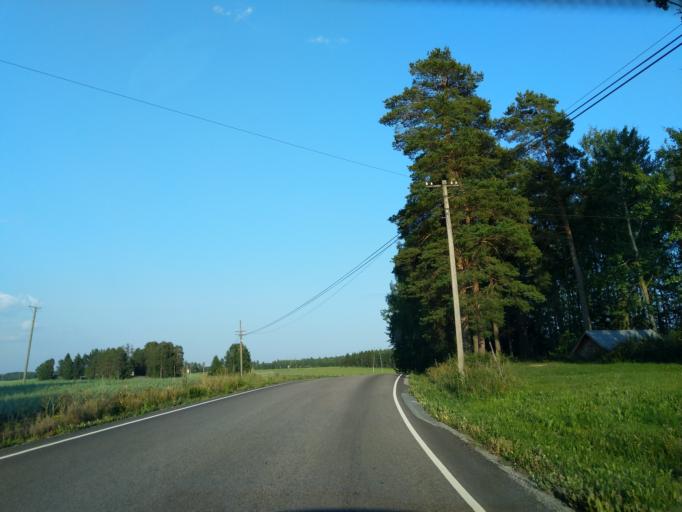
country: FI
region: Satakunta
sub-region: Pohjois-Satakunta
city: Kankaanpaeae
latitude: 61.8198
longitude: 22.3117
